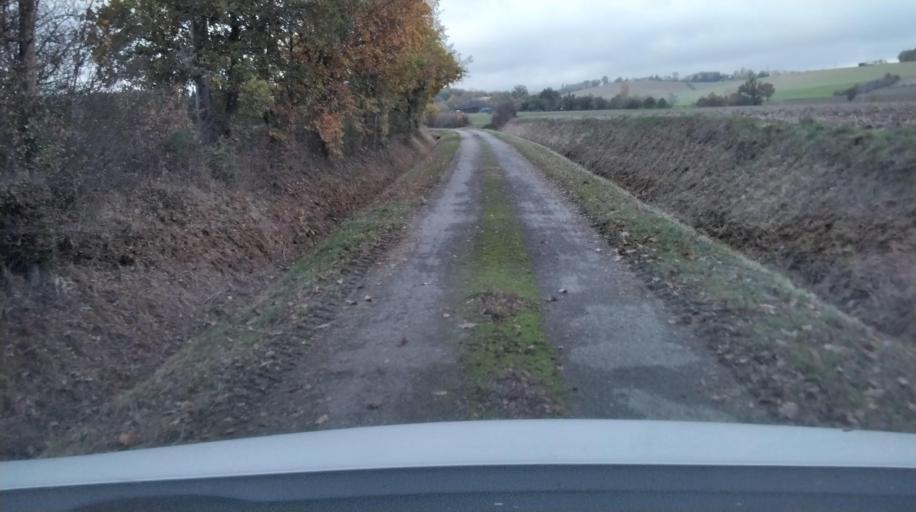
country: FR
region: Midi-Pyrenees
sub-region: Departement de la Haute-Garonne
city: Le Fousseret
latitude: 43.2704
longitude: 1.0309
